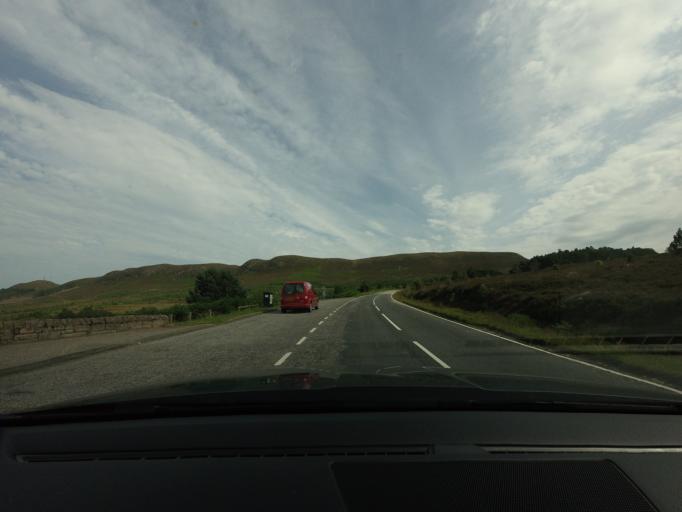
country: GB
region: Scotland
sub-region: Highland
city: Alness
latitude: 57.8411
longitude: -4.2714
